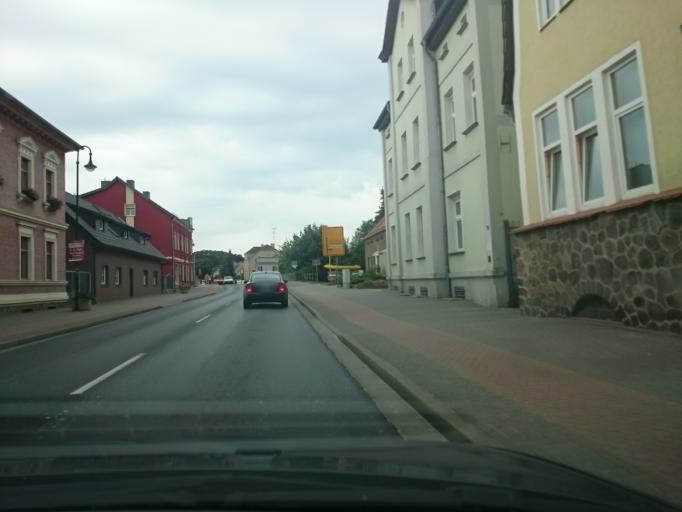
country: DE
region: Brandenburg
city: Furstenberg
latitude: 53.1823
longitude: 13.1447
